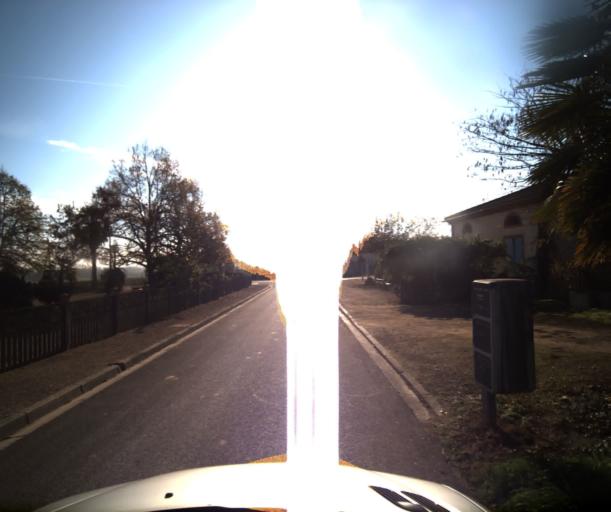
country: FR
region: Midi-Pyrenees
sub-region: Departement du Tarn-et-Garonne
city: Lafrancaise
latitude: 44.1012
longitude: 1.2947
